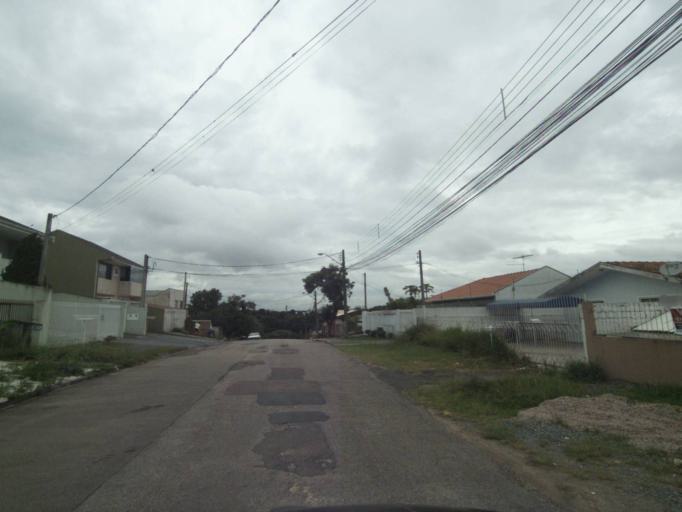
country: BR
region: Parana
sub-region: Curitiba
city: Curitiba
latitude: -25.4750
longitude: -49.3317
